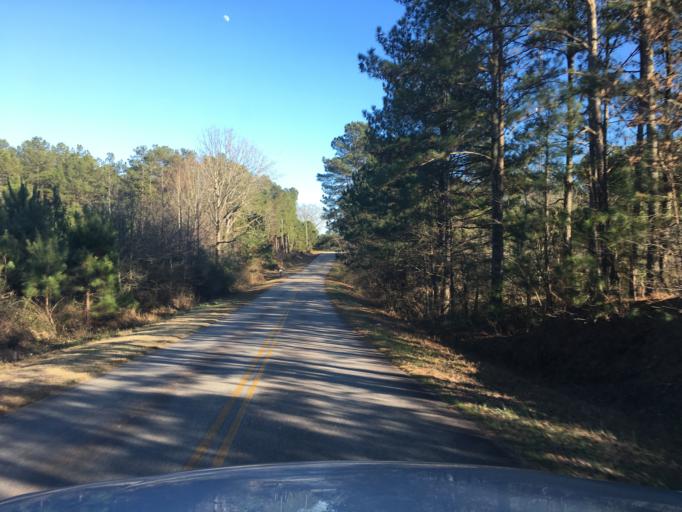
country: US
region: Georgia
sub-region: Carroll County
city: Carrollton
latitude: 33.4391
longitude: -85.1103
